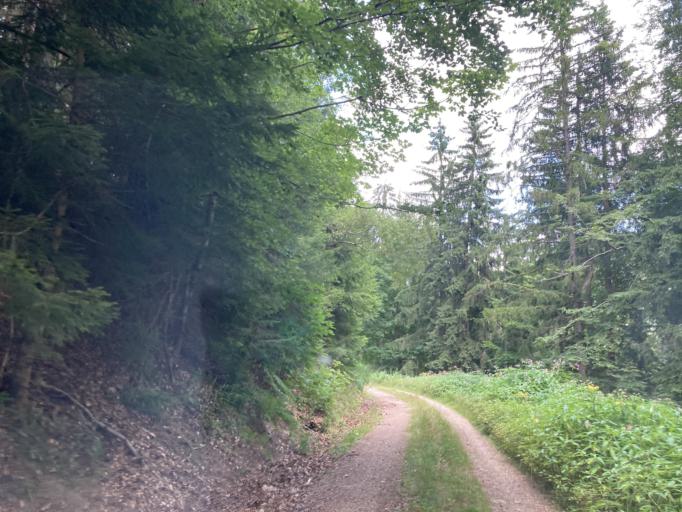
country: DE
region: Baden-Wuerttemberg
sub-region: Freiburg Region
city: Schonach im Schwarzwald
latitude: 48.1552
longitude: 8.1567
